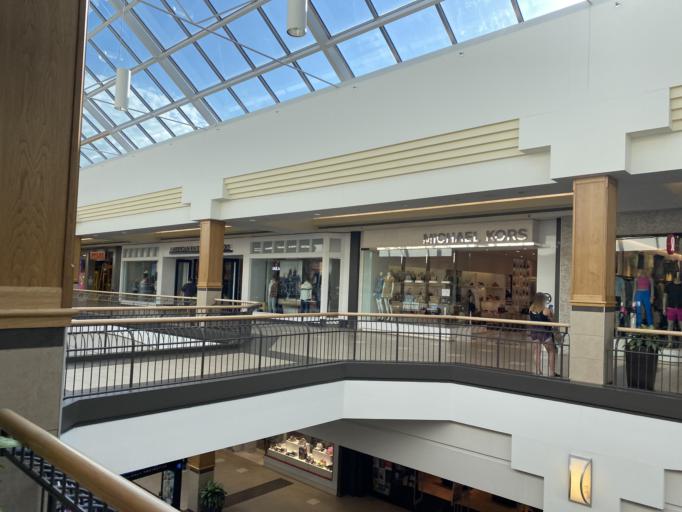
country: CA
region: Manitoba
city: Winnipeg
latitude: 49.8847
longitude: -97.1990
